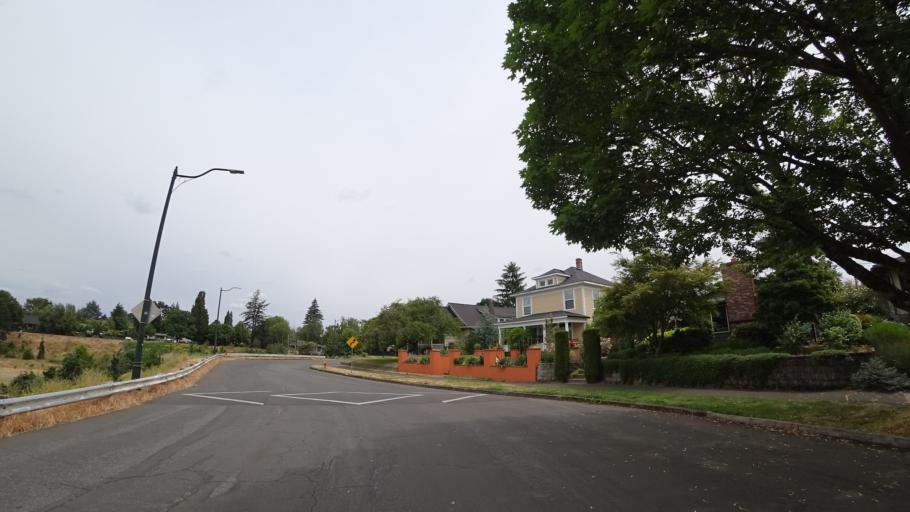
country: US
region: Oregon
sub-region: Multnomah County
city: Portland
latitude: 45.5640
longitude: -122.6980
